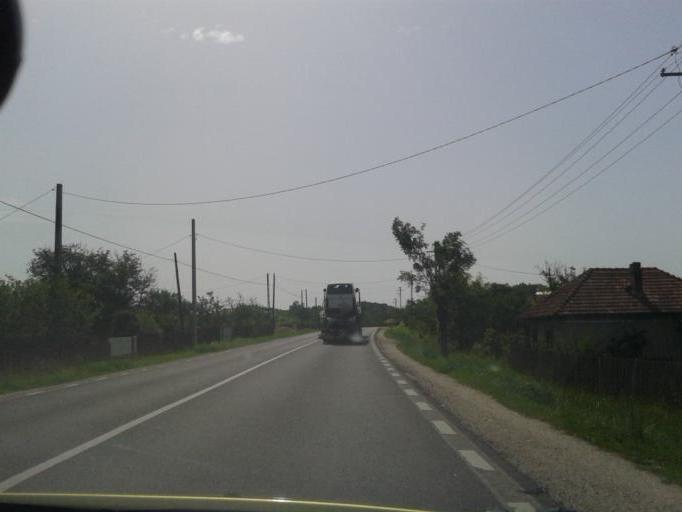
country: RO
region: Arges
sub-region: Comuna Cotmeana
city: Cotmeana
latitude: 44.9832
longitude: 24.6507
